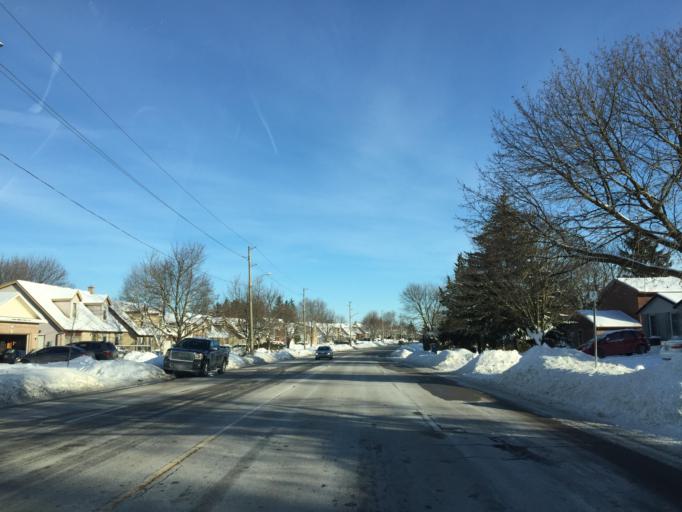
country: CA
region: Ontario
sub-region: Wellington County
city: Guelph
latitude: 43.5122
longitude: -80.2322
